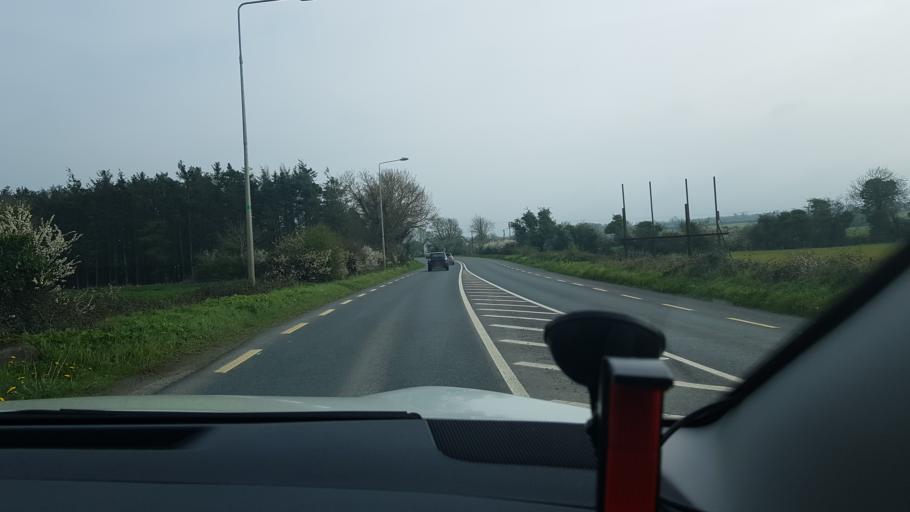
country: IE
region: Leinster
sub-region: An Mhi
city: Stamullin
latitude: 53.6639
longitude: -6.2720
